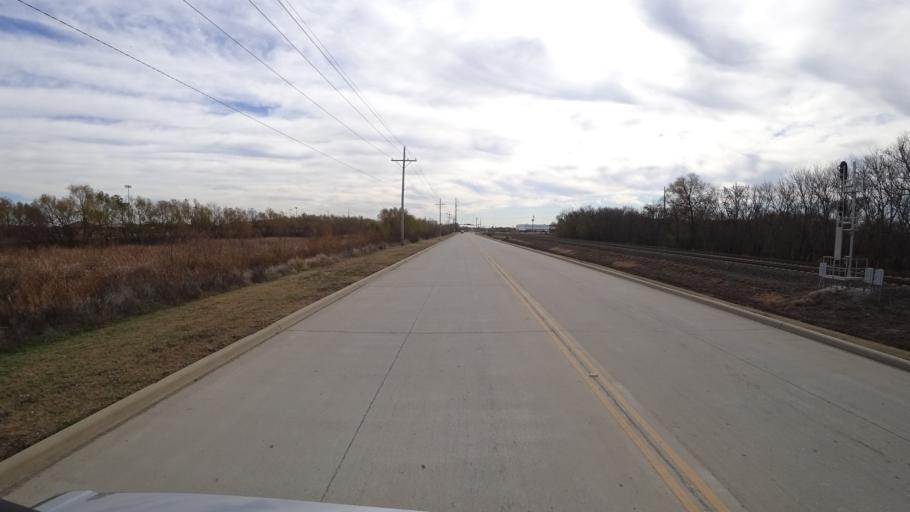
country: US
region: Texas
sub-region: Denton County
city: Lewisville
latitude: 33.0293
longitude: -96.9746
